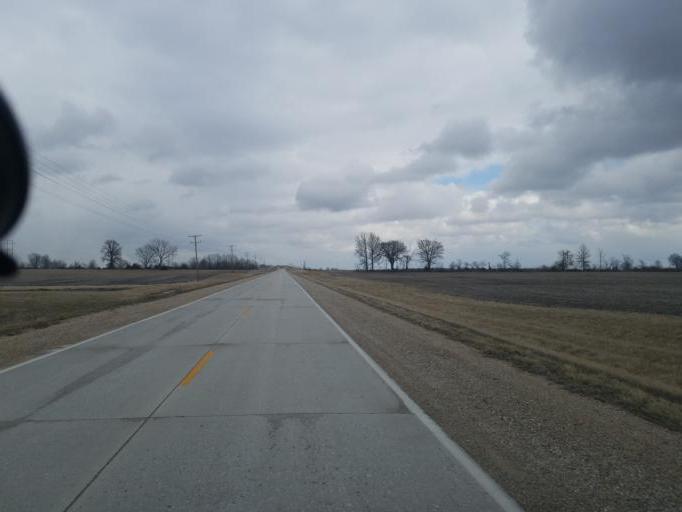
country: US
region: Missouri
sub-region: Boone County
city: Hallsville
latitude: 39.2464
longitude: -92.3117
